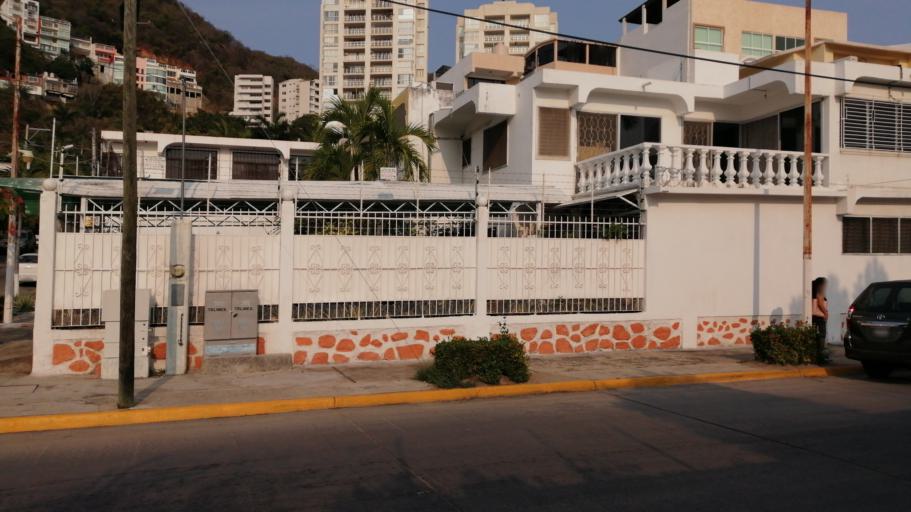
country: MX
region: Guerrero
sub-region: Acapulco de Juarez
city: Colonia Alborada
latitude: 16.8499
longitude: -99.8444
